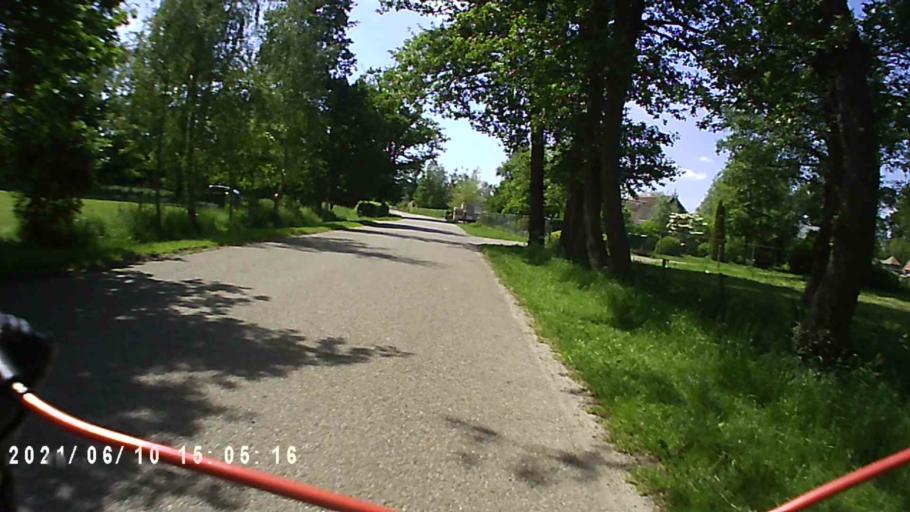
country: NL
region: Friesland
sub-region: Gemeente Achtkarspelen
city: Surhuizum
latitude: 53.1954
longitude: 6.2207
